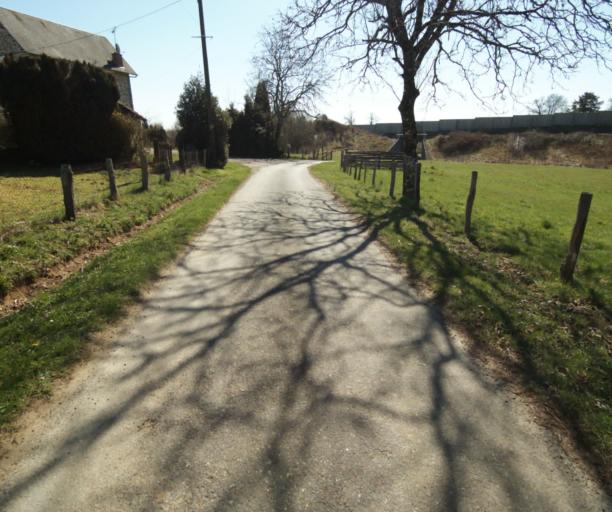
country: FR
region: Limousin
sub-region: Departement de la Correze
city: Saint-Clement
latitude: 45.3103
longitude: 1.6987
